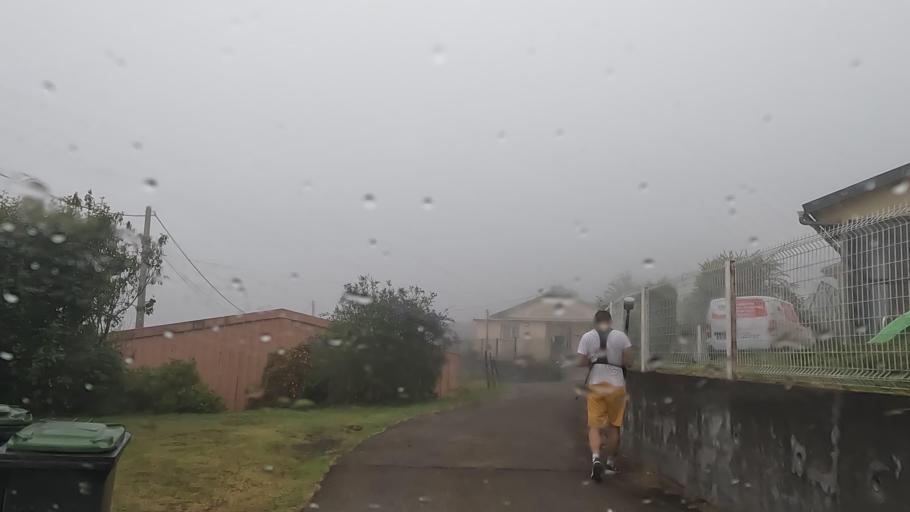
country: RE
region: Reunion
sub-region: Reunion
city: Le Tampon
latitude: -21.2079
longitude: 55.5882
